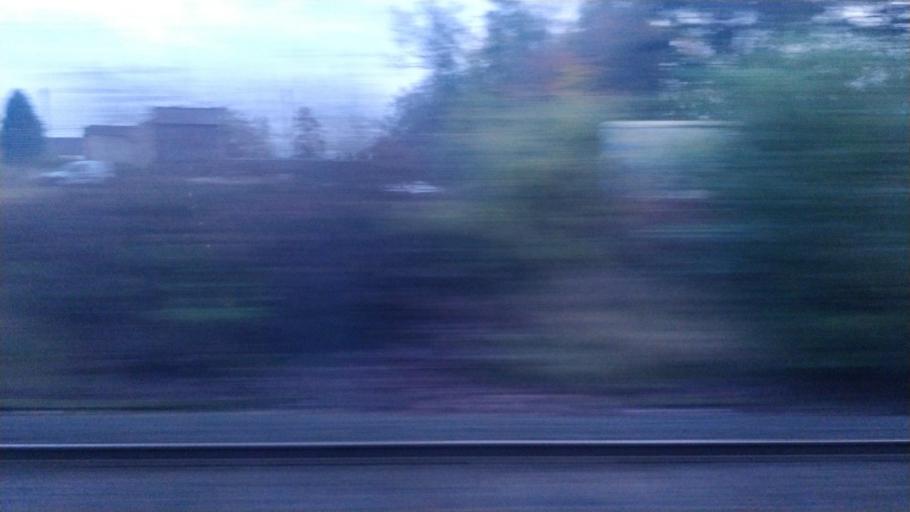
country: GB
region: England
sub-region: Borough of Wigan
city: Hindley
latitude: 53.5436
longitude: -2.5585
